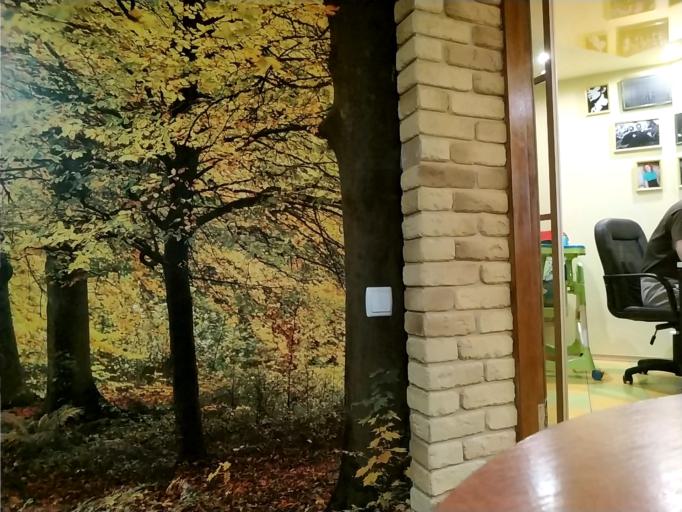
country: RU
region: Tverskaya
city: Staraya Toropa
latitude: 56.3362
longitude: 31.8683
